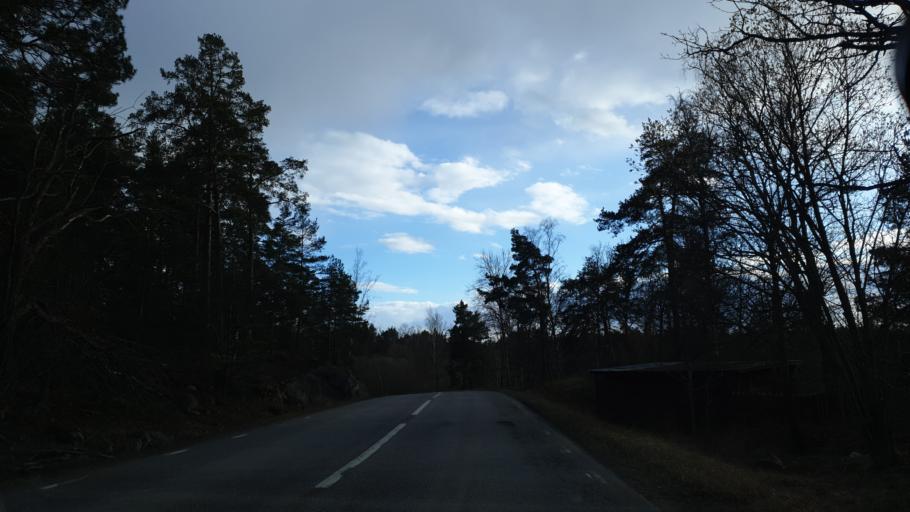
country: SE
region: Stockholm
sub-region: Varmdo Kommun
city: Holo
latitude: 59.3522
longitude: 18.7035
